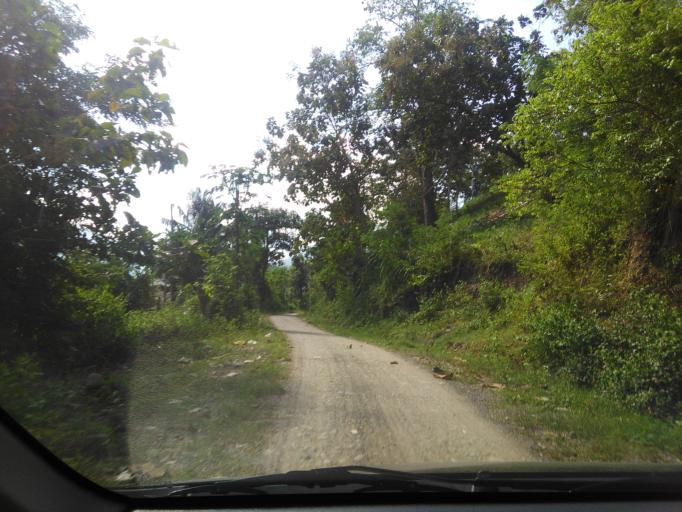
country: ID
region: South Sulawesi
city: Enrekang
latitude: -3.5106
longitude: 119.7346
